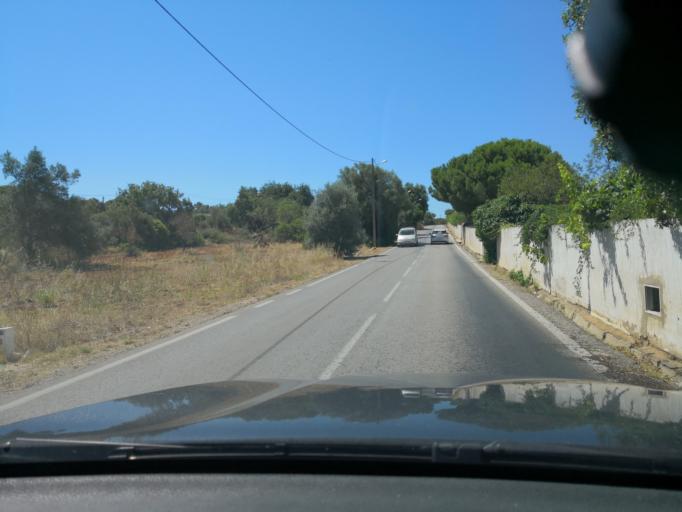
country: PT
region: Faro
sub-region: Loule
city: Vilamoura
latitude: 37.1082
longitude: -8.0965
